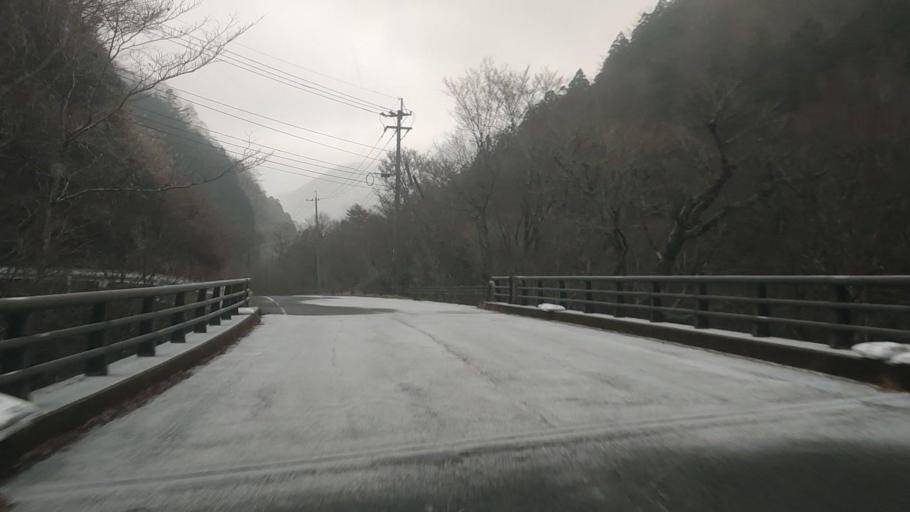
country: JP
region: Kumamoto
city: Matsubase
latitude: 32.5633
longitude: 130.9137
